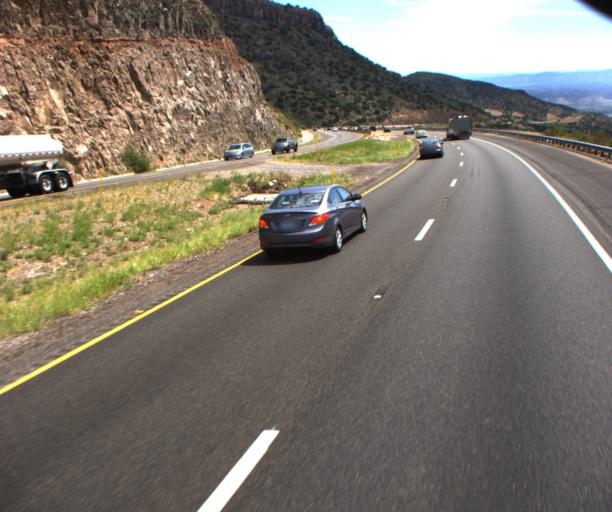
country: US
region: Arizona
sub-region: Yavapai County
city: Camp Verde
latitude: 34.5311
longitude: -111.9432
